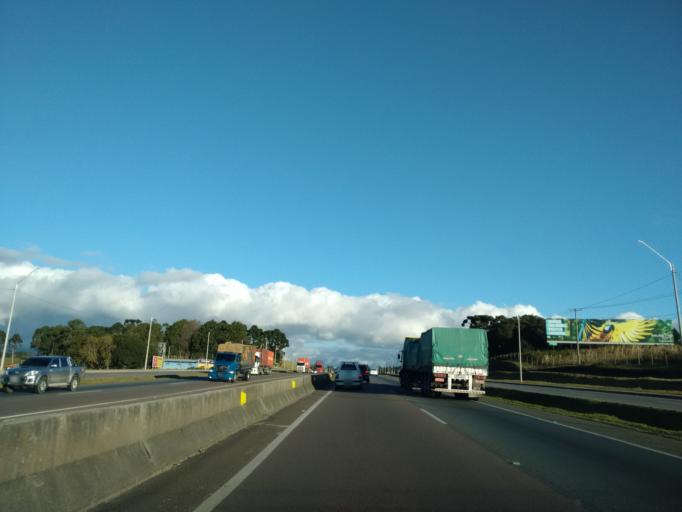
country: BR
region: Parana
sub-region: Sao Jose Dos Pinhais
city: Sao Jose dos Pinhais
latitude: -25.6726
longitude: -49.1514
